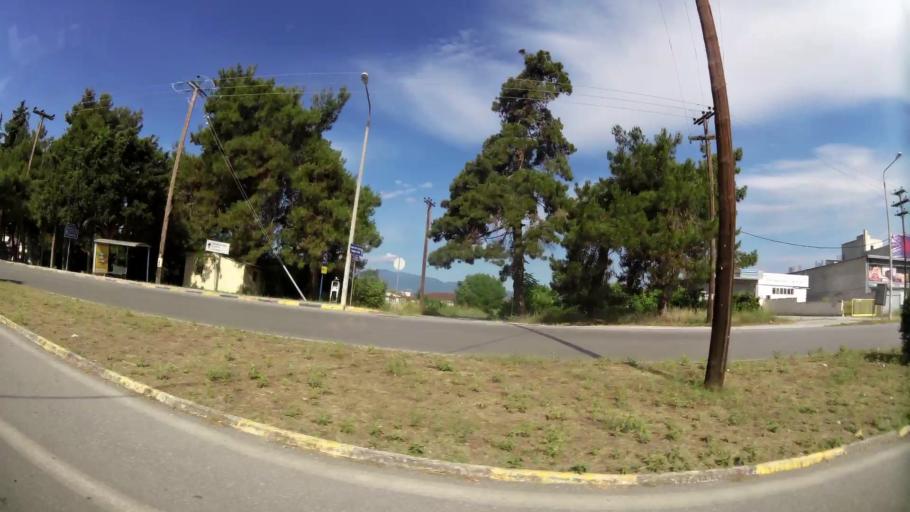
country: GR
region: Central Macedonia
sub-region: Nomos Pierias
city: Katerini
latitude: 40.2815
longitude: 22.5180
